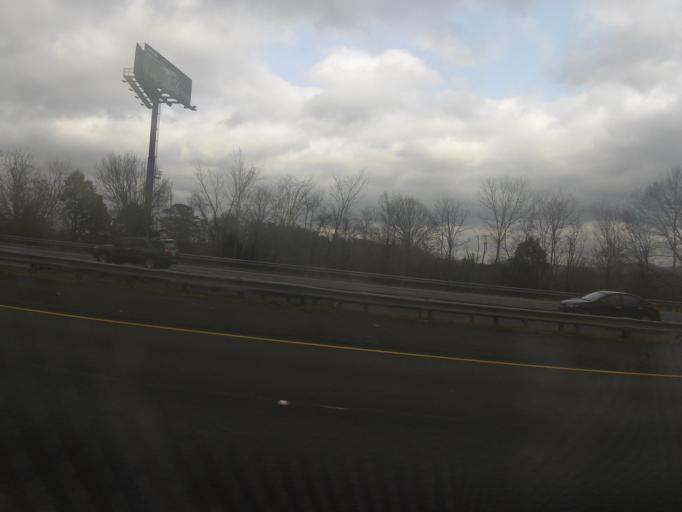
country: US
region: Georgia
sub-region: Catoosa County
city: Indian Springs
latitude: 34.9618
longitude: -85.1841
